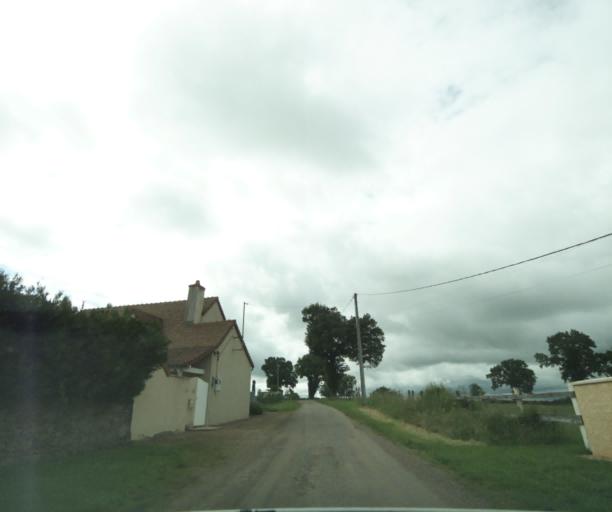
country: FR
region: Bourgogne
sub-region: Departement de Saone-et-Loire
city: Charolles
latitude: 46.4224
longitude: 4.3039
